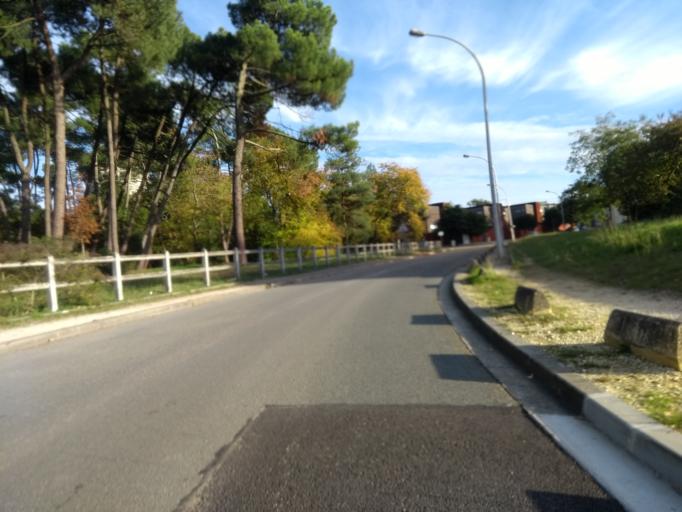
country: FR
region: Aquitaine
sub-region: Departement de la Gironde
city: Talence
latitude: 44.8002
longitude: -0.6167
